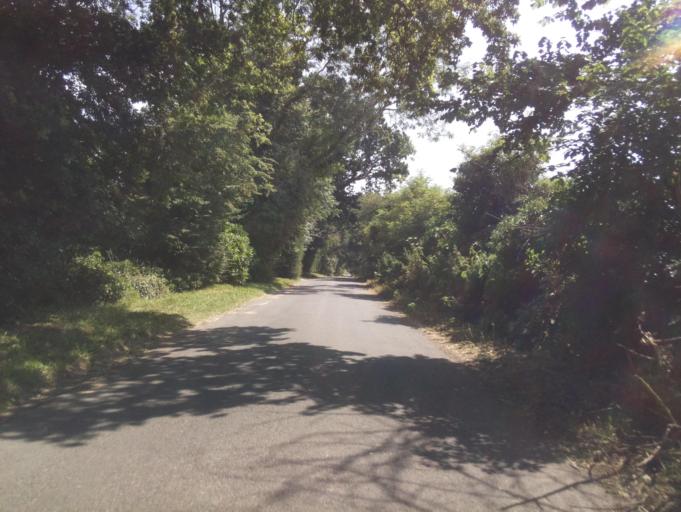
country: GB
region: England
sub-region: Gloucestershire
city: Donnington
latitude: 51.9514
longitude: -1.7182
